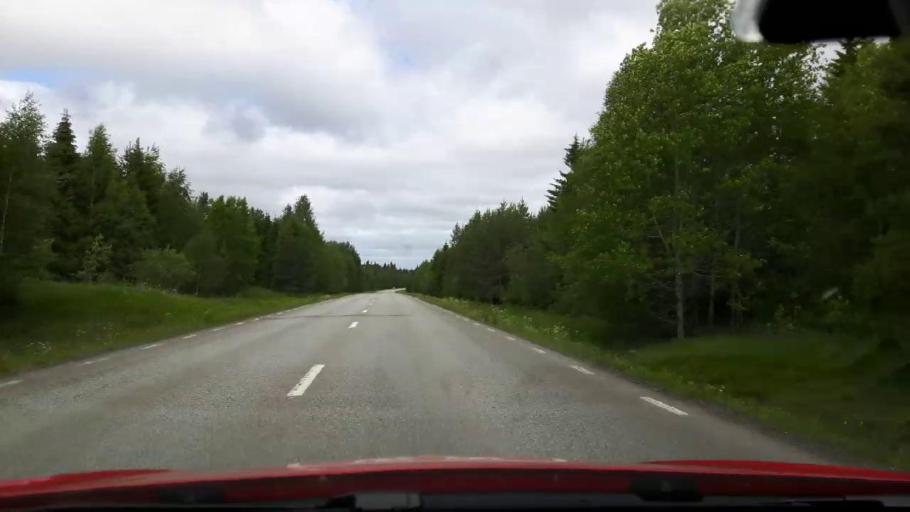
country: SE
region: Jaemtland
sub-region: Krokoms Kommun
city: Krokom
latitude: 63.3713
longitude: 14.5073
